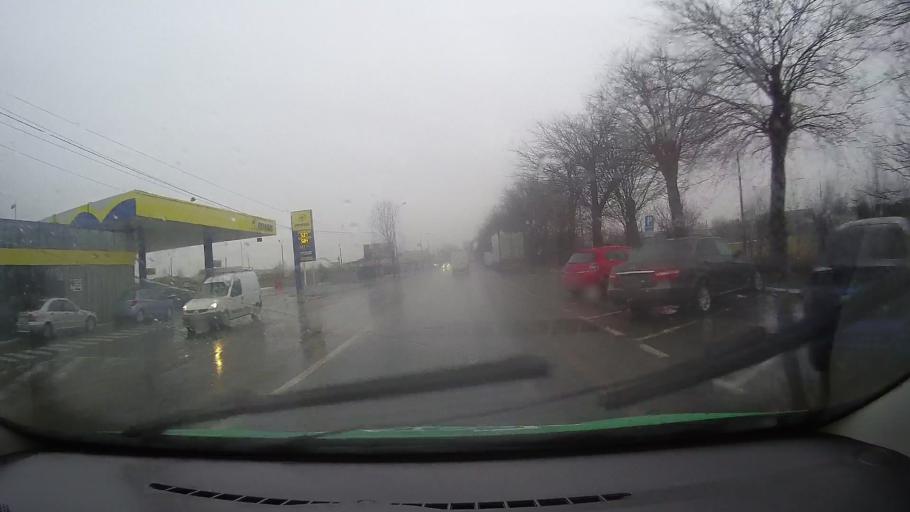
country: RO
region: Sibiu
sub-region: Municipiul Sibiu
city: Sibiu
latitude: 45.8180
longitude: 24.1499
